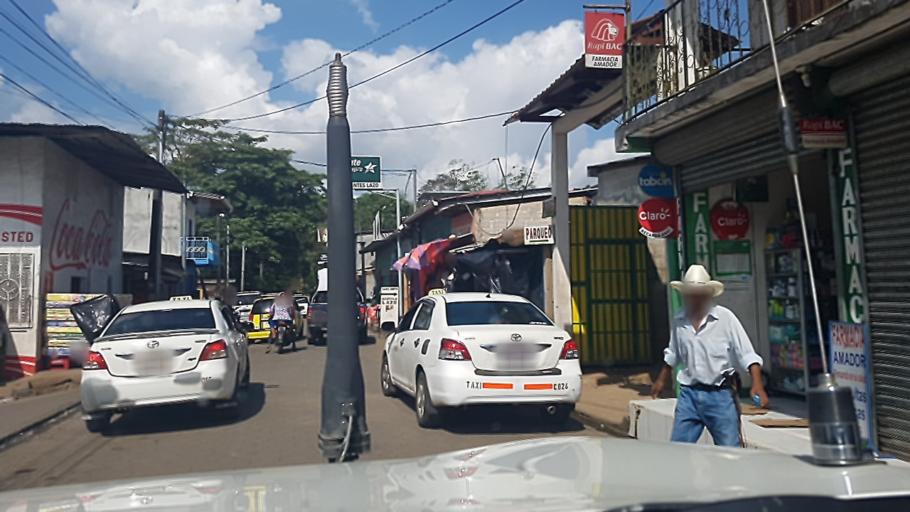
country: NI
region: Atlantico Sur
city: Nueva Guinea
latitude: 11.6897
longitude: -84.4515
